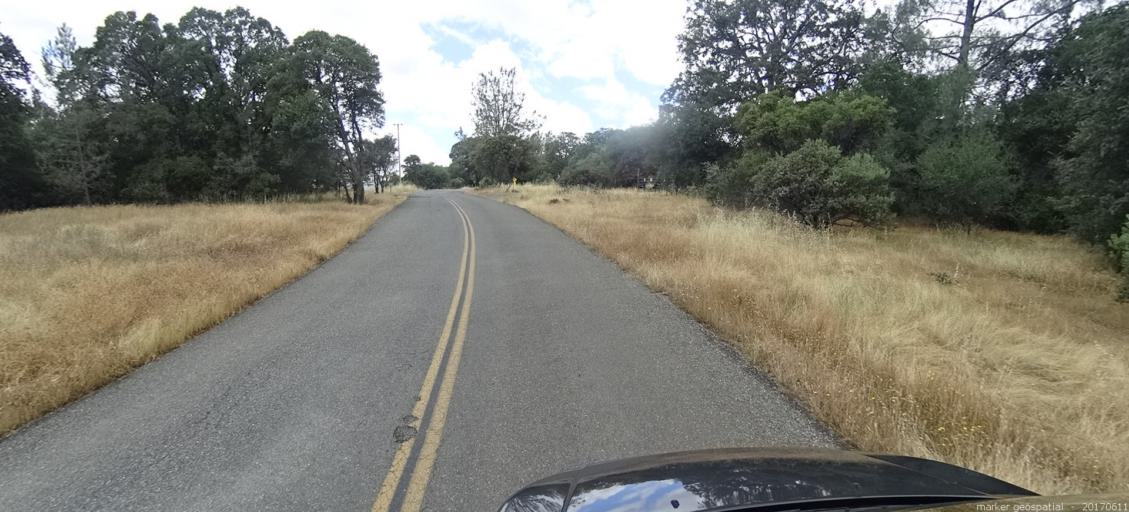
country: US
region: California
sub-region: Butte County
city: Berry Creek
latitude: 39.6467
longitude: -121.5356
